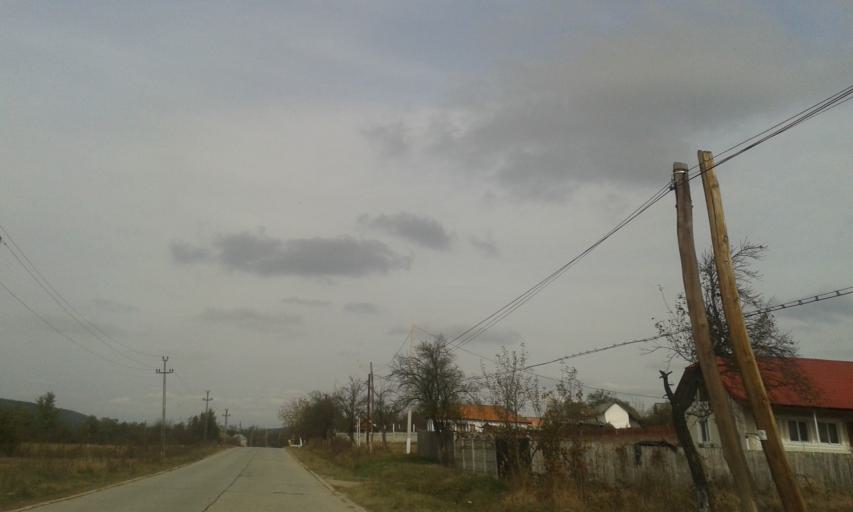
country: RO
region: Gorj
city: Logresti
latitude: 44.8639
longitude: 23.7014
